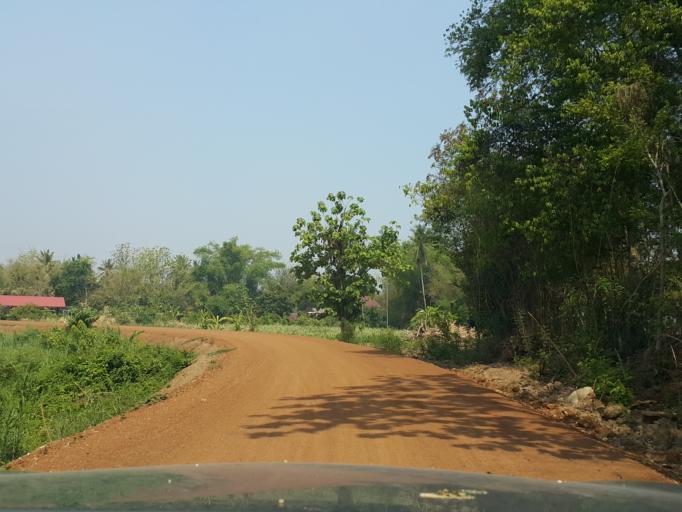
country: TH
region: Sukhothai
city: Thung Saliam
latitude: 17.3161
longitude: 99.5567
